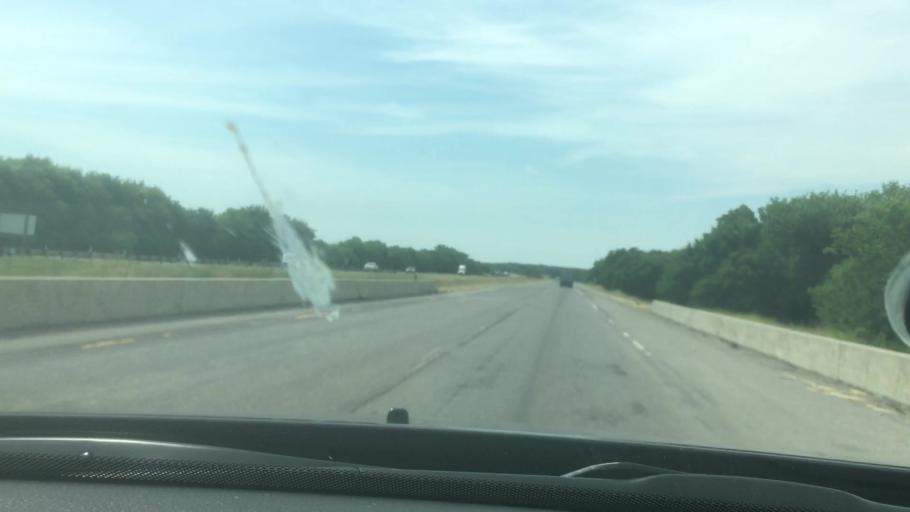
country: US
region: Oklahoma
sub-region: Murray County
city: Davis
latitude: 34.5329
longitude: -97.1875
